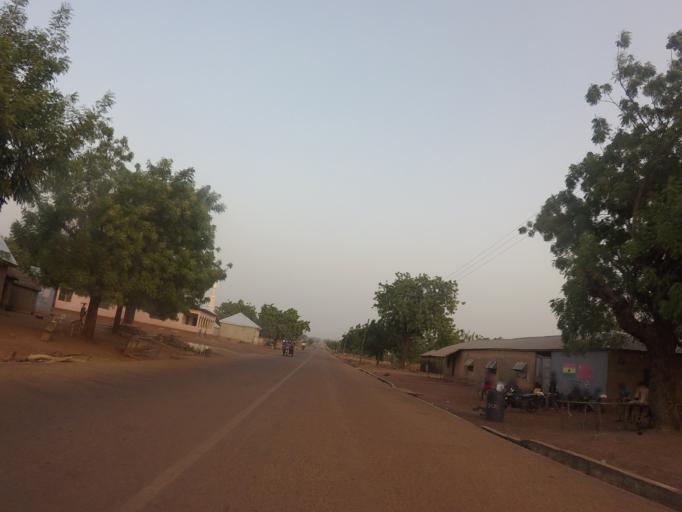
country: GH
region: Northern
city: Tamale
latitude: 9.4446
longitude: -1.1145
